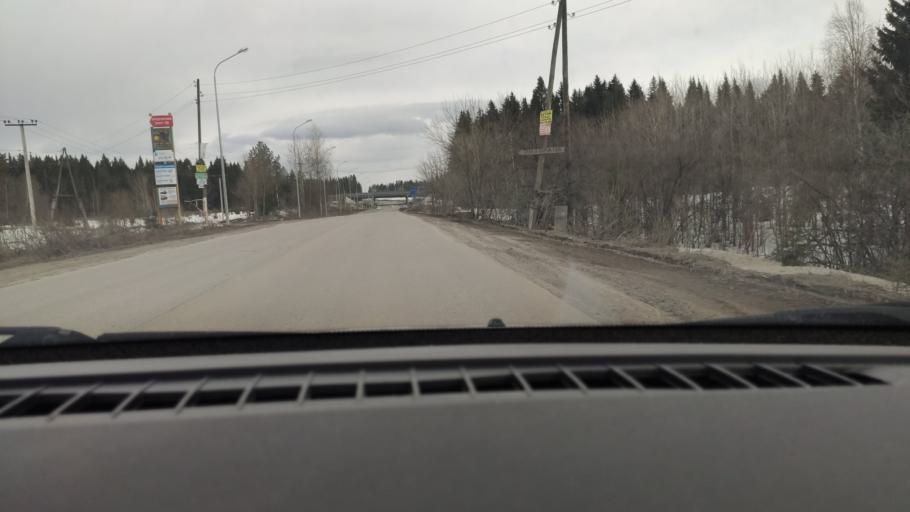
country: RU
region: Perm
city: Ferma
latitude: 57.9528
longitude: 56.3827
